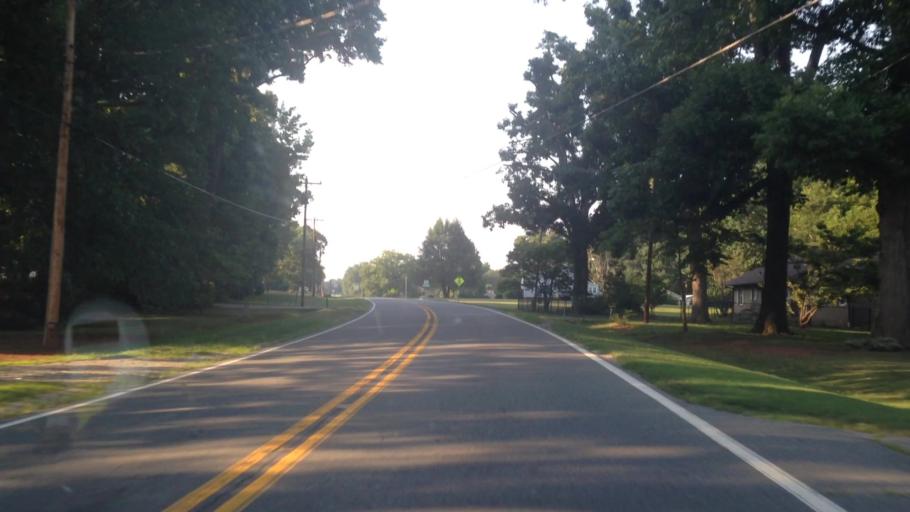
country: US
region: North Carolina
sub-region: Rockingham County
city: Reidsville
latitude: 36.3139
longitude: -79.7154
